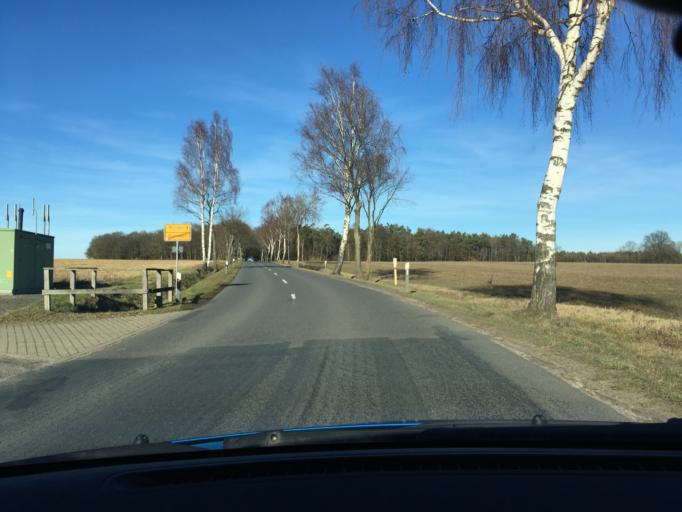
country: DE
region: Lower Saxony
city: Schwienau
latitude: 52.9824
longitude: 10.4456
